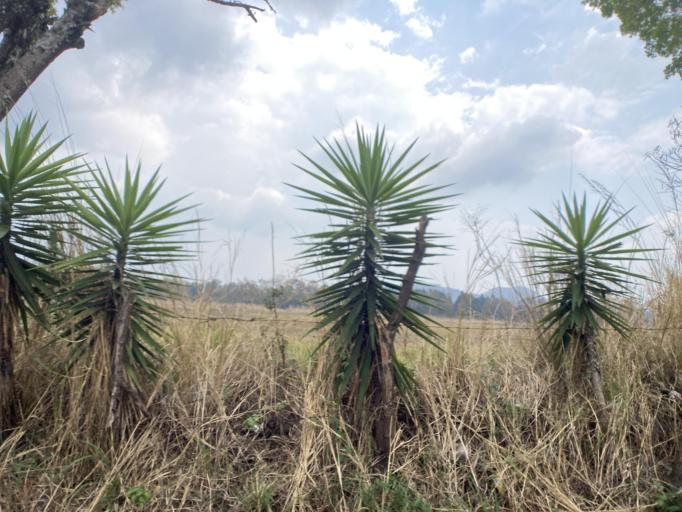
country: GT
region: Guatemala
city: Fraijanes
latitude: 14.3892
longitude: -90.4877
